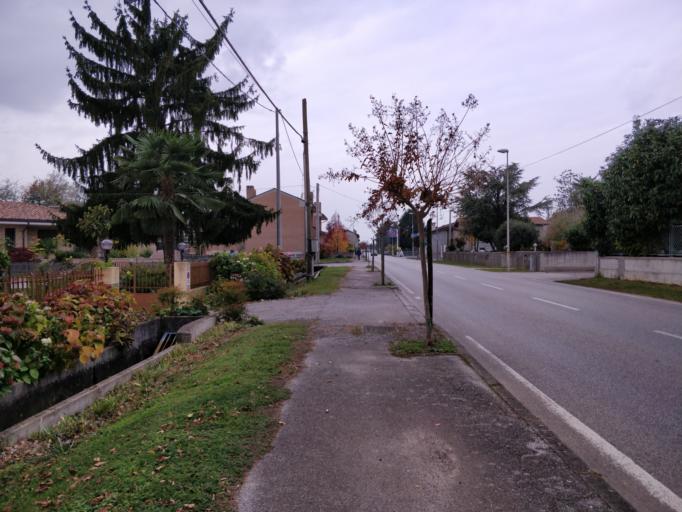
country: IT
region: Friuli Venezia Giulia
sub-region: Provincia di Udine
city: Bertiolo
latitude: 45.9417
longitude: 13.0606
